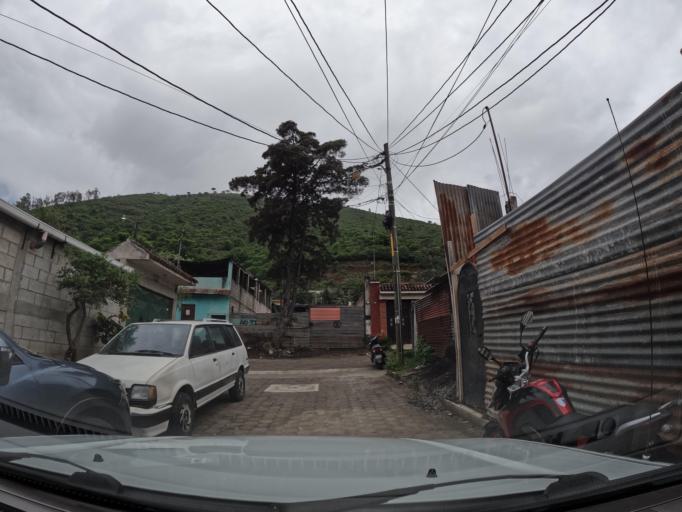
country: GT
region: Sacatepequez
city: Jocotenango
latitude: 14.5845
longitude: -90.7497
